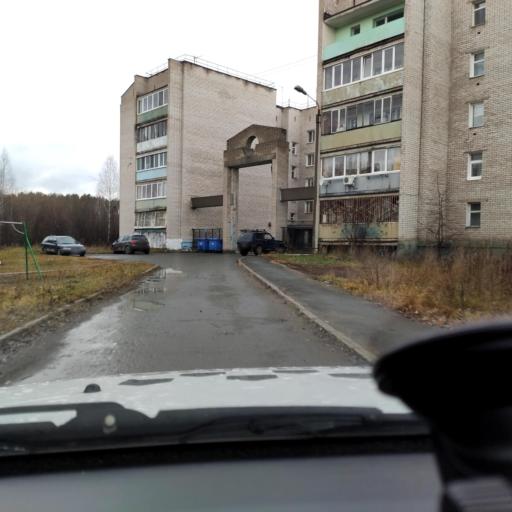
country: RU
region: Perm
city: Perm
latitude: 58.0567
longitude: 56.2813
